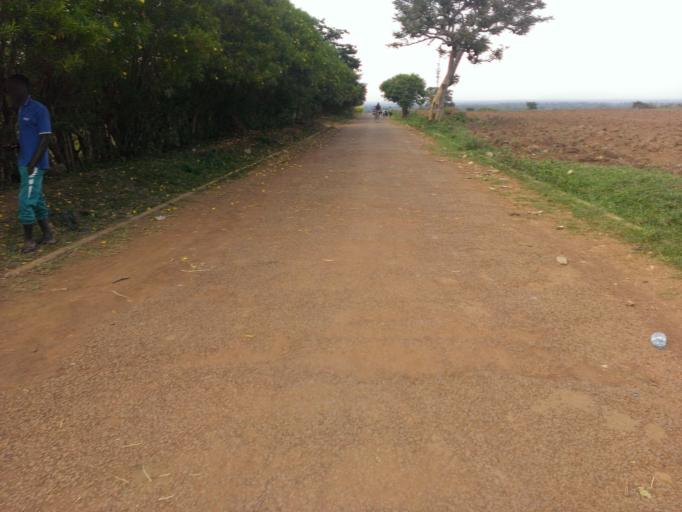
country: UG
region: Eastern Region
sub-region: Busia District
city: Busia
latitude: 0.5420
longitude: 34.0259
